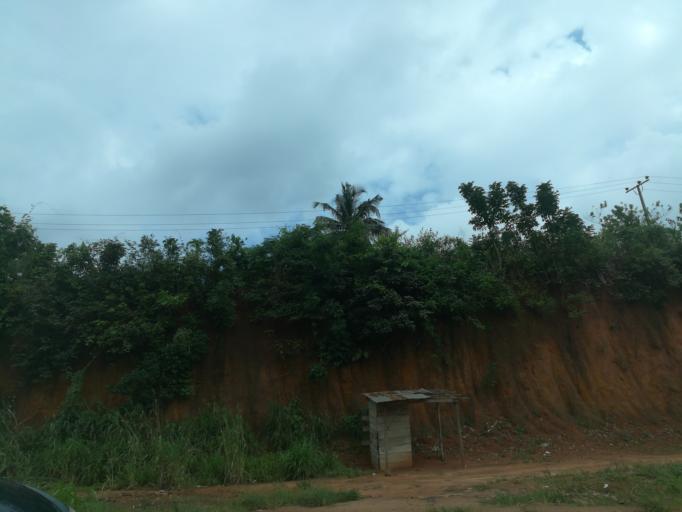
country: NG
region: Lagos
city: Ikorodu
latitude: 6.6526
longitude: 3.5779
